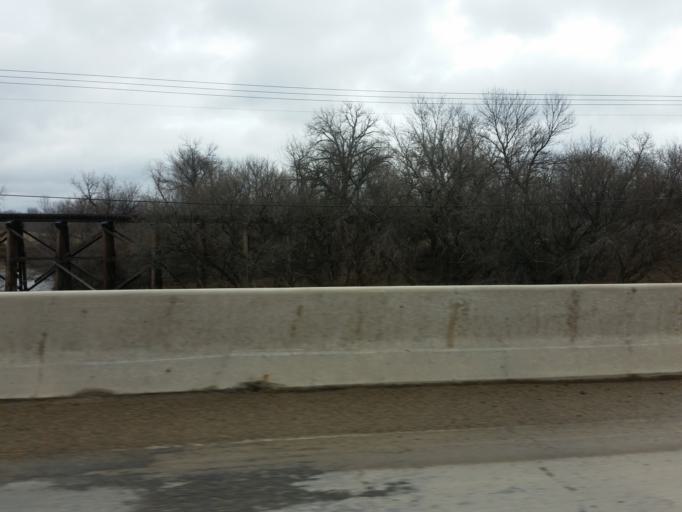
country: US
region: North Dakota
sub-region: Traill County
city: Mayville
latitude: 47.4886
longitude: -97.3227
